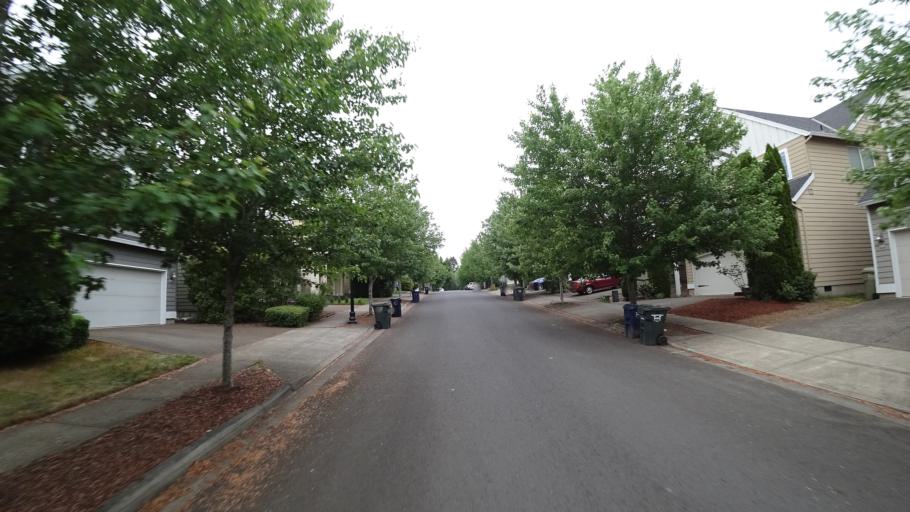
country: US
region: Oregon
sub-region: Washington County
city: Rockcreek
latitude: 45.5217
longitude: -122.8923
